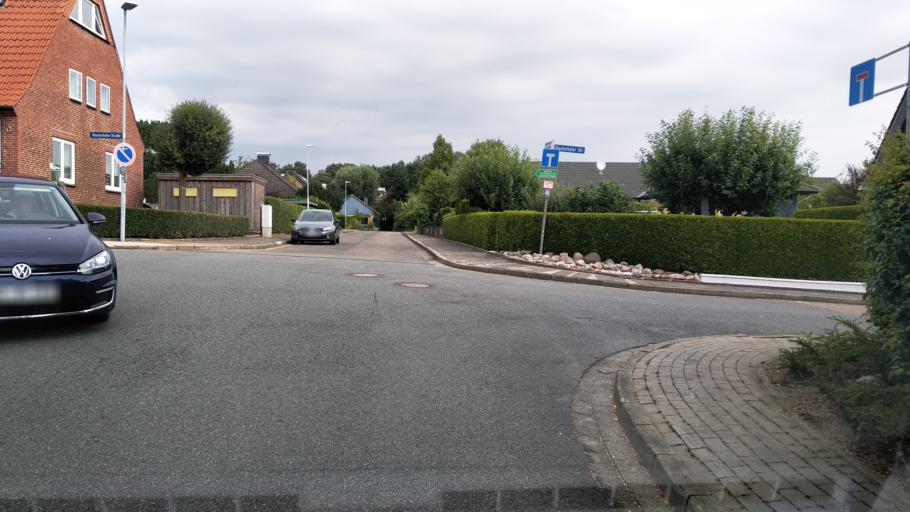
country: DE
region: Schleswig-Holstein
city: Schleswig
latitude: 54.5174
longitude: 9.5799
